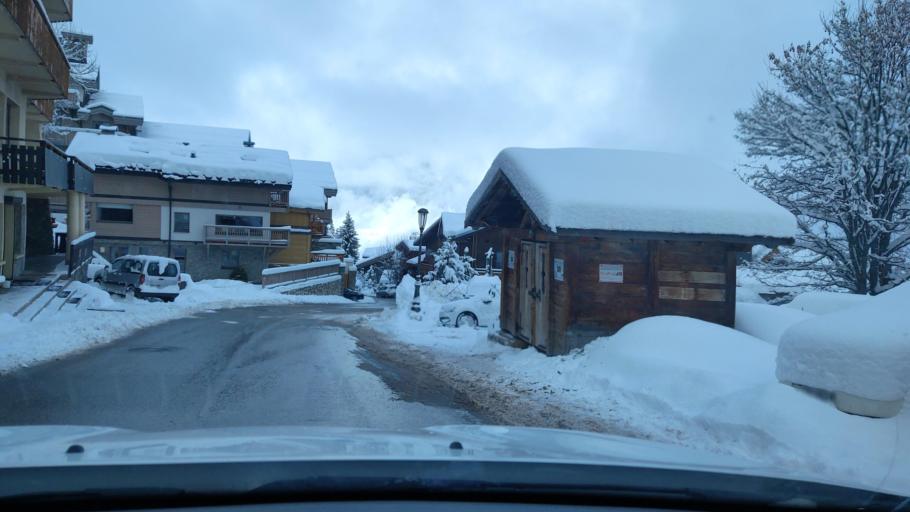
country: FR
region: Rhone-Alpes
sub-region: Departement de la Savoie
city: Courchevel
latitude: 45.4222
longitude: 6.6430
